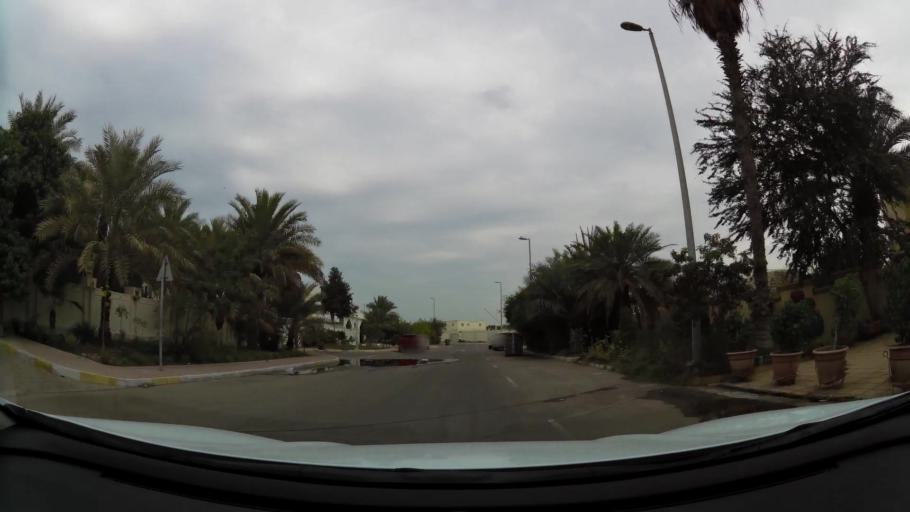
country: AE
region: Abu Dhabi
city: Abu Dhabi
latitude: 24.4346
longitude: 54.3851
